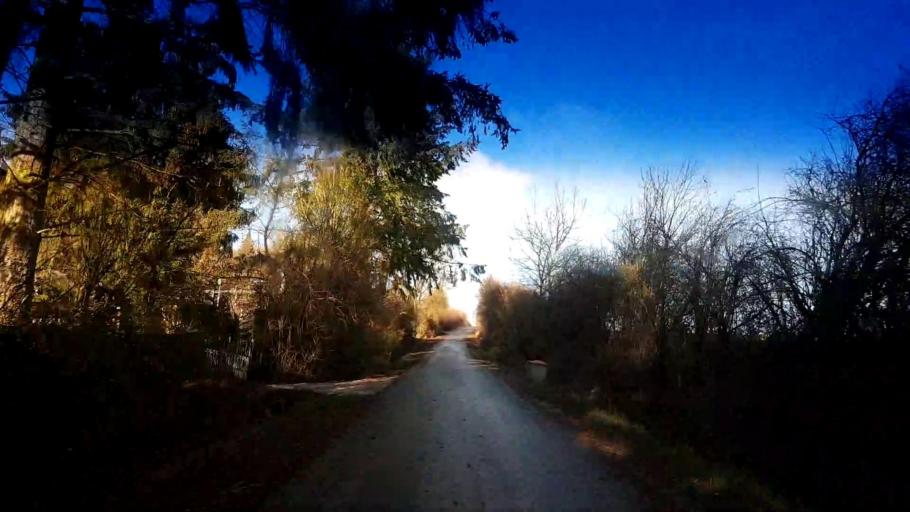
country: DE
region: Bavaria
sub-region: Upper Franconia
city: Pettstadt
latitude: 49.8365
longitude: 10.9212
